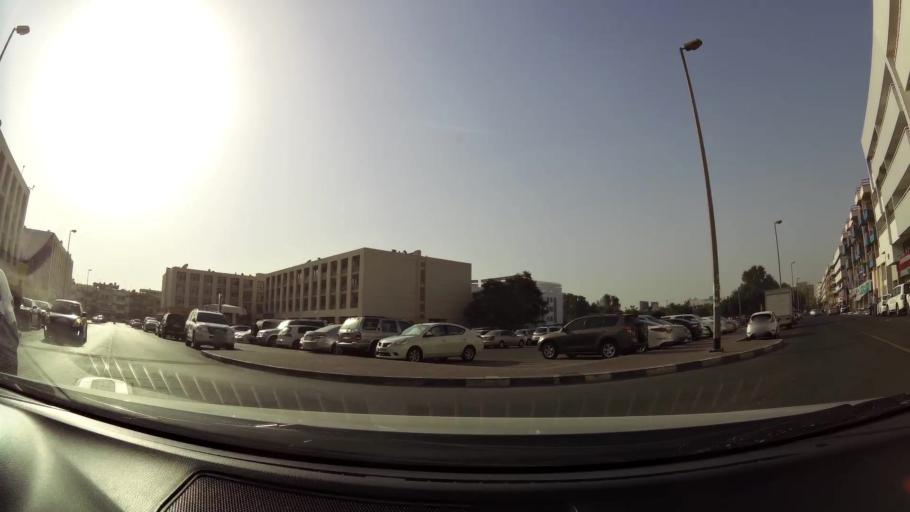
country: AE
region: Ash Shariqah
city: Sharjah
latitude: 25.2410
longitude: 55.3053
